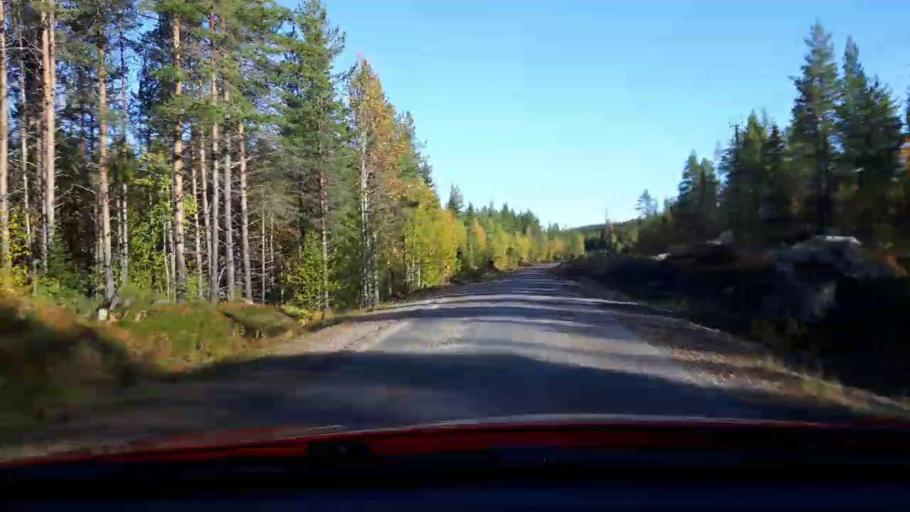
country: SE
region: Jaemtland
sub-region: Stroemsunds Kommun
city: Stroemsund
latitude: 64.3899
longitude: 15.1503
